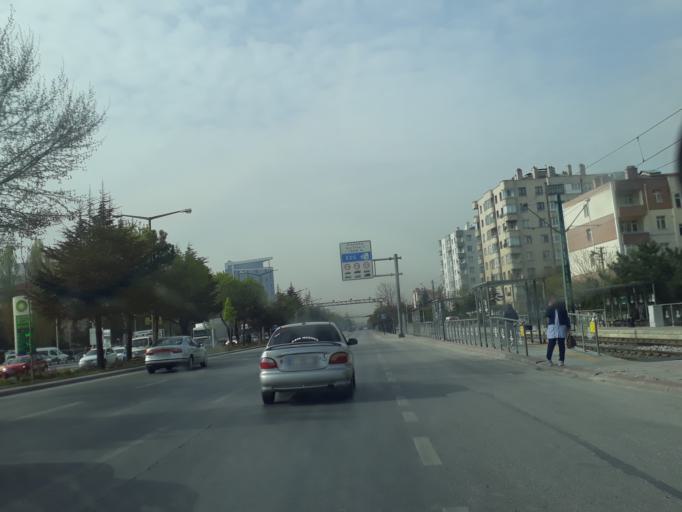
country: TR
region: Konya
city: Selcuklu
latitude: 37.9412
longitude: 32.5116
